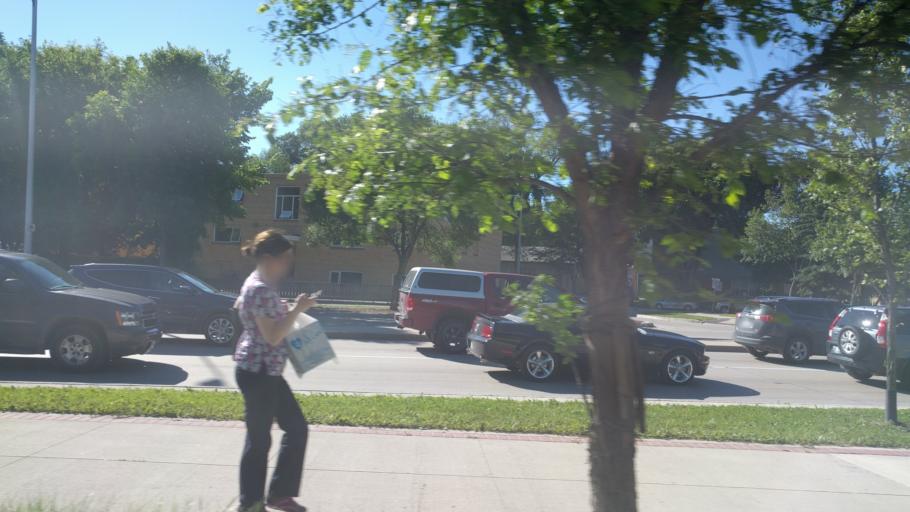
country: CA
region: Manitoba
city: Winnipeg
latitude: 49.8832
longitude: -97.1321
